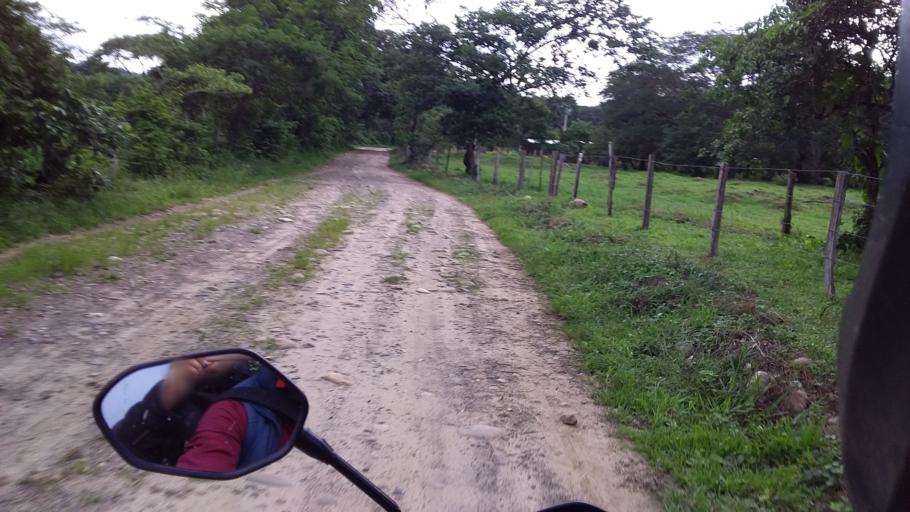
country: CO
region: Casanare
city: Nunchia
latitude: 5.6335
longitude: -72.2000
